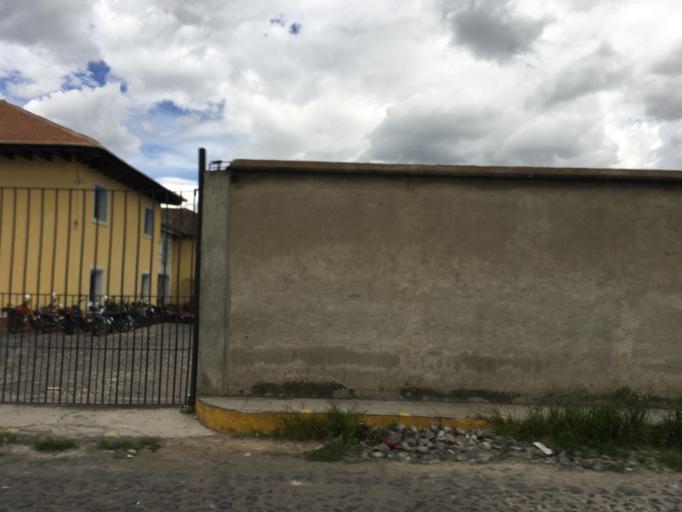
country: GT
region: Sacatepequez
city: Antigua Guatemala
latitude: 14.5568
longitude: -90.7402
